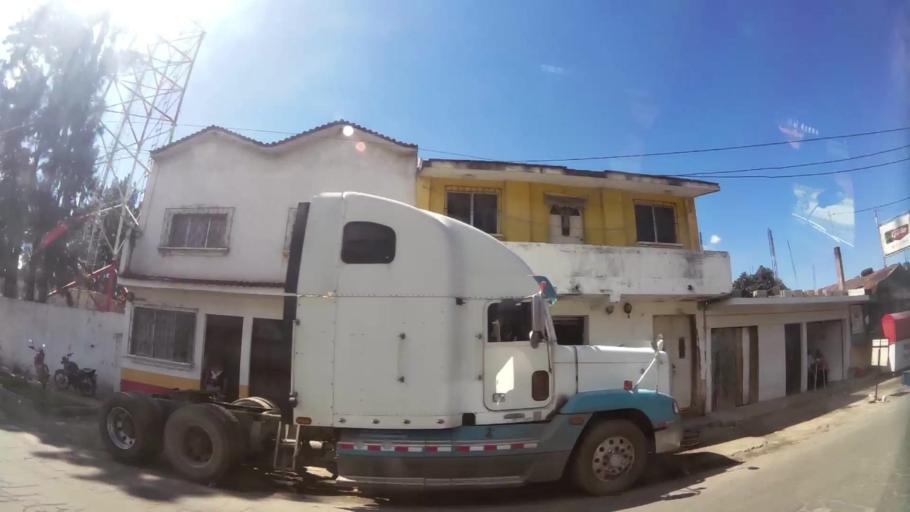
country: GT
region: Guatemala
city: Villa Canales
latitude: 14.4795
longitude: -90.5332
